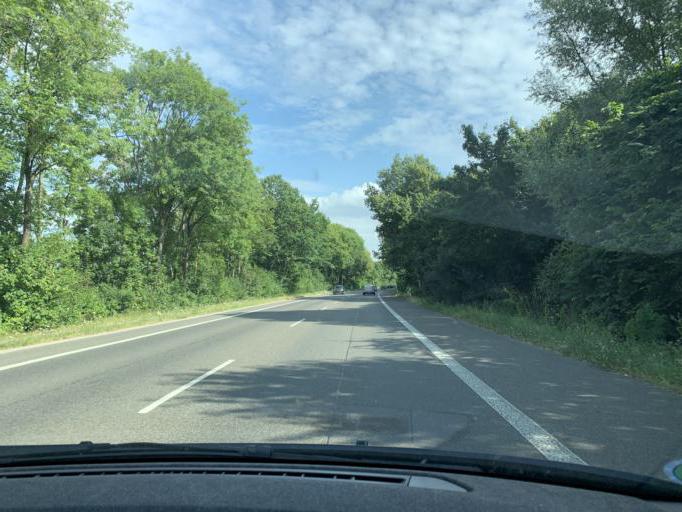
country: DE
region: North Rhine-Westphalia
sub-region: Regierungsbezirk Koln
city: Inden
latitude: 50.8832
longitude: 6.4085
